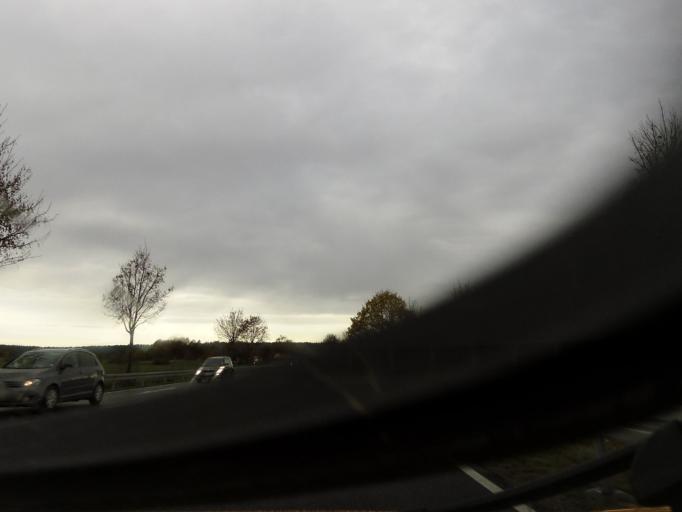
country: DE
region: Saxony-Anhalt
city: Gardelegen
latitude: 52.5485
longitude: 11.3649
